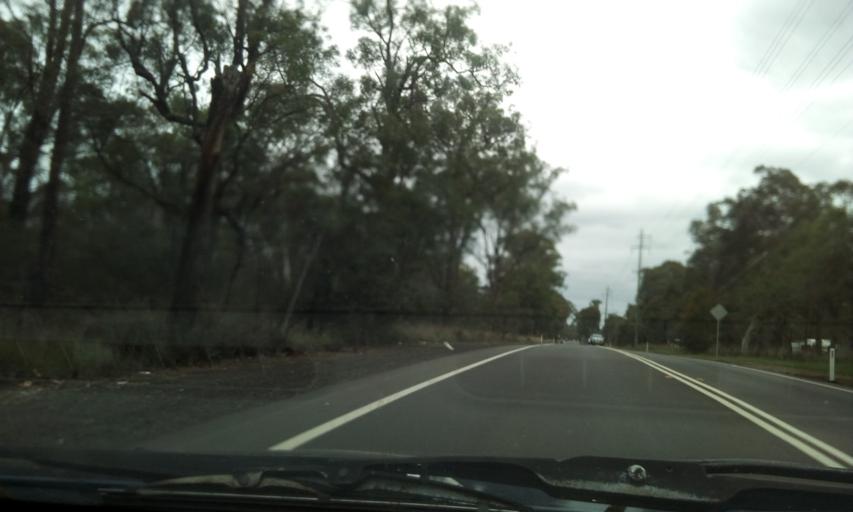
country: AU
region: New South Wales
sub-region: Hawkesbury
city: South Windsor
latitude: -33.6519
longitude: 150.7747
